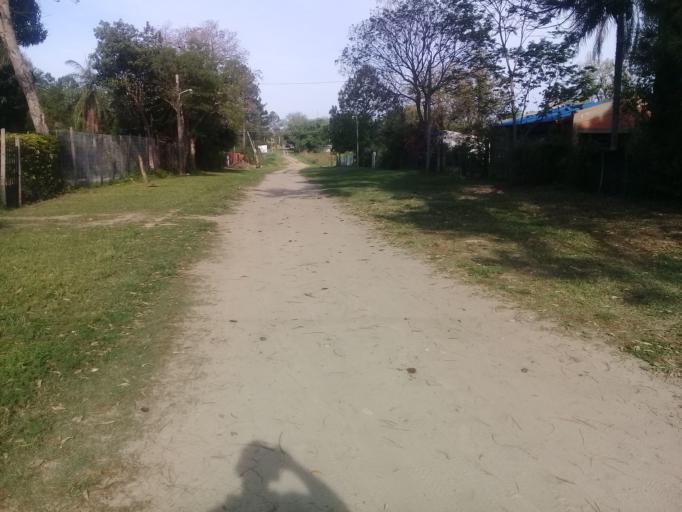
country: AR
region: Corrientes
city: San Luis del Palmar
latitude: -27.4542
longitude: -58.6589
